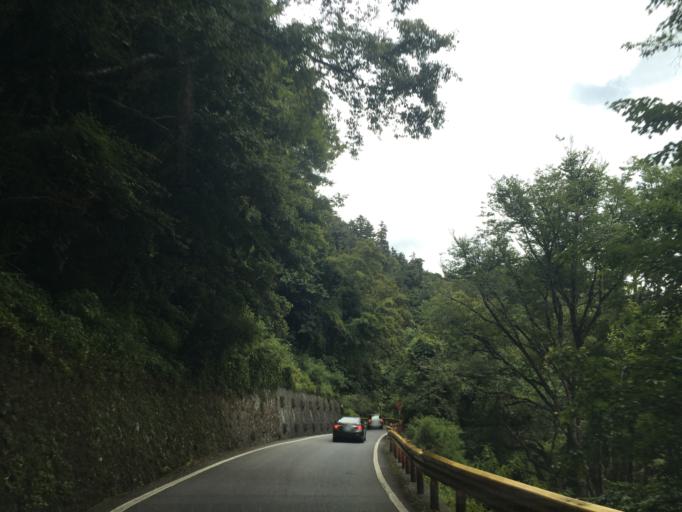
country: TW
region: Taiwan
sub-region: Hualien
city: Hualian
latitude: 24.1745
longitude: 121.3811
